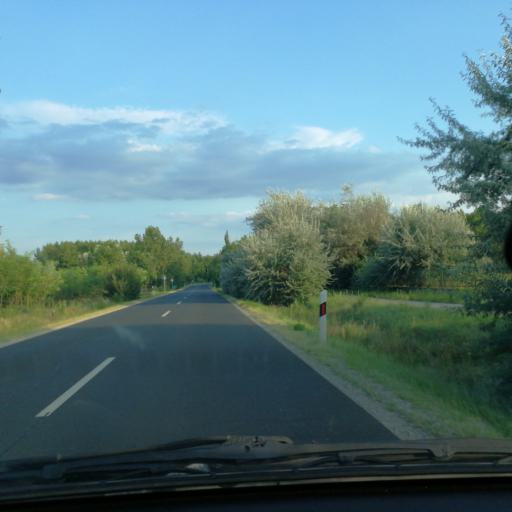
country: HU
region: Bacs-Kiskun
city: Jaszszentlaszlo
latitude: 46.5357
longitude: 19.7385
